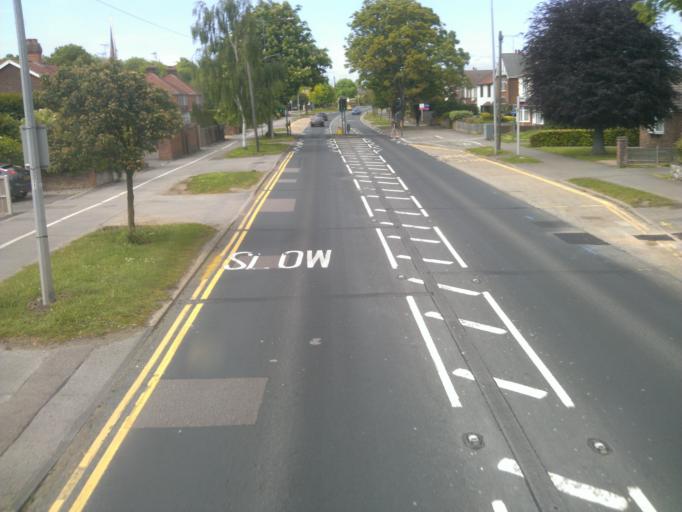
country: GB
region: England
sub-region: Essex
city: Colchester
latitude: 51.9049
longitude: 0.9242
